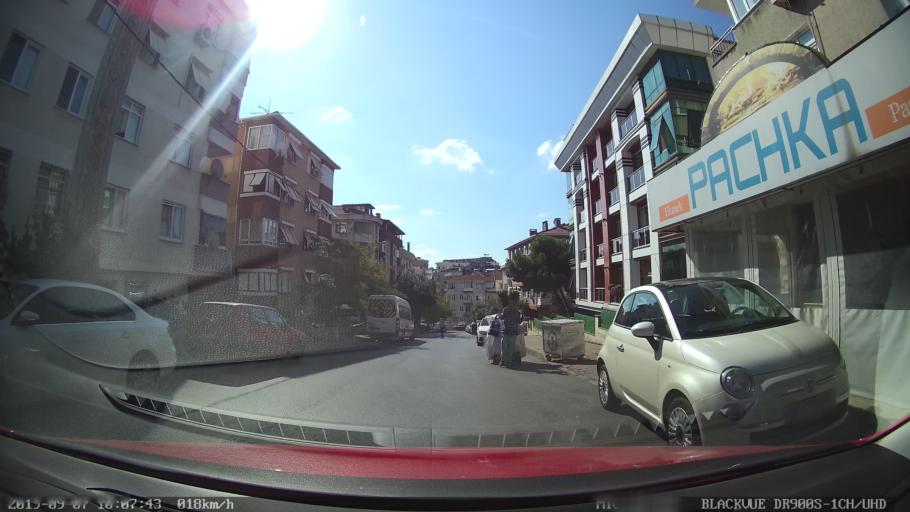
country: TR
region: Istanbul
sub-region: Atasehir
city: Atasehir
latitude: 40.9491
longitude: 29.1122
